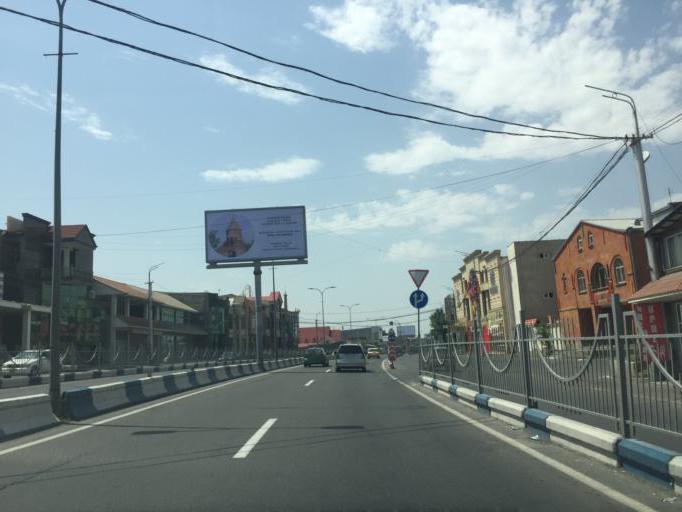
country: AM
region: Ararat
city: Argavand
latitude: 40.1583
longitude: 44.4318
